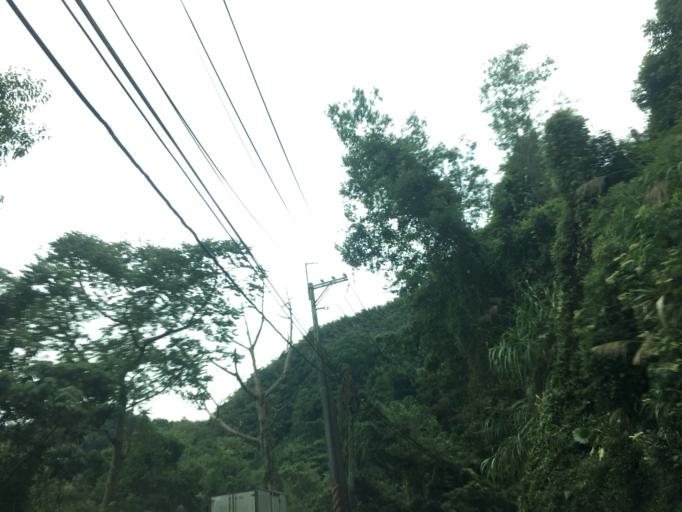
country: TW
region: Taiwan
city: Lugu
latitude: 23.5442
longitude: 120.7078
